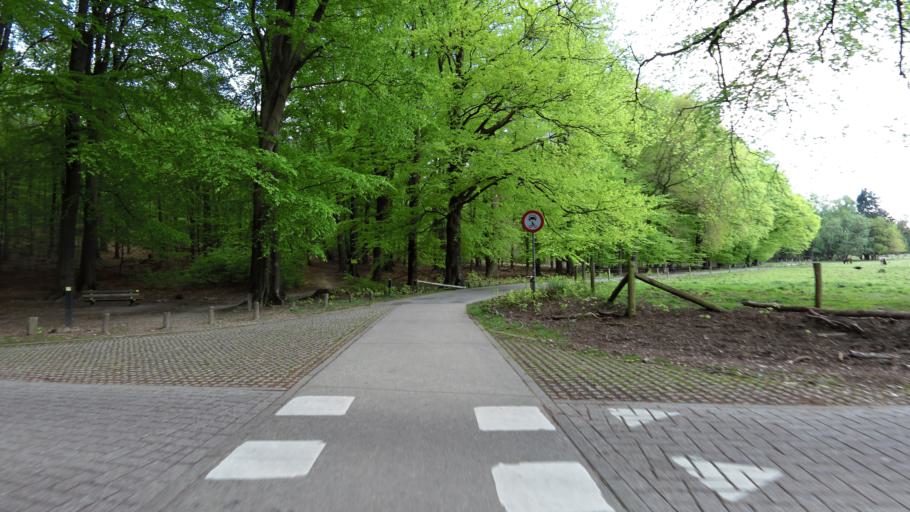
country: NL
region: Gelderland
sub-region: Gemeente Rheden
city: De Steeg
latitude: 52.0300
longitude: 6.0392
